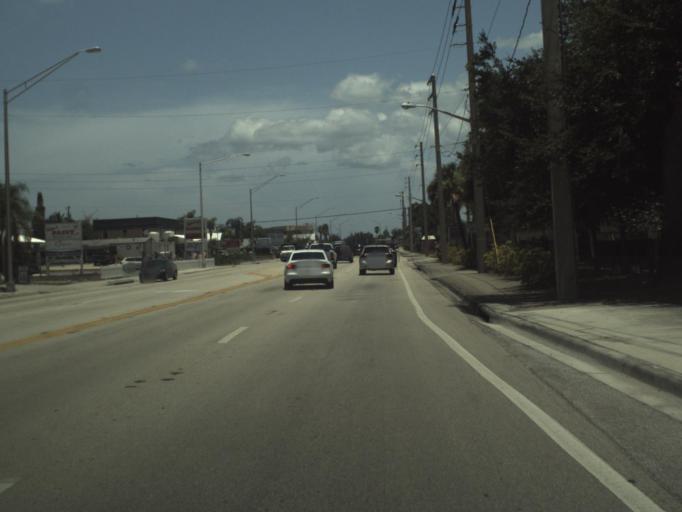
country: US
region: Florida
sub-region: Martin County
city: Palm City
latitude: 27.1722
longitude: -80.2690
